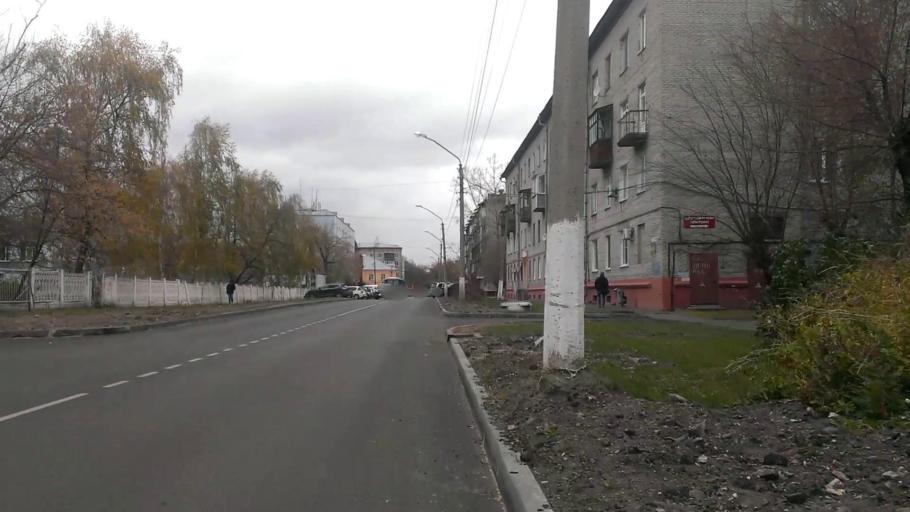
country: RU
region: Altai Krai
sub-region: Gorod Barnaulskiy
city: Barnaul
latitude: 53.3514
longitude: 83.7693
